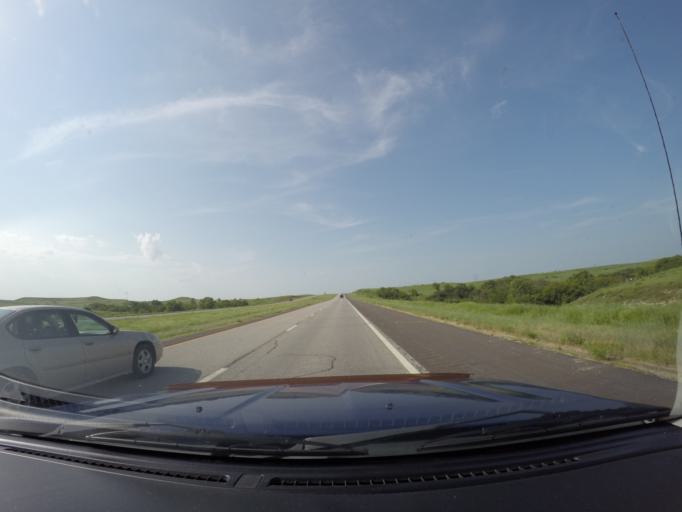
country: US
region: Kansas
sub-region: Riley County
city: Manhattan
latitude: 39.0890
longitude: -96.5381
